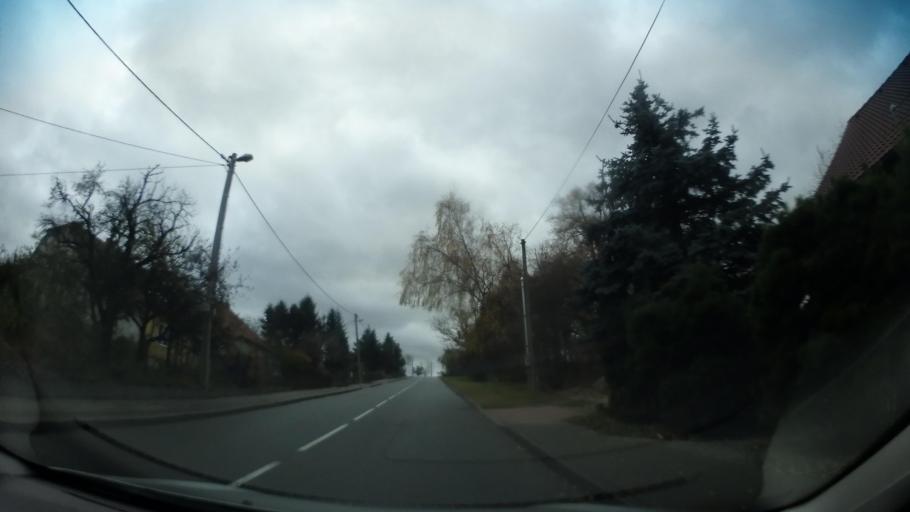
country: CZ
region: Vysocina
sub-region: Okres Zd'ar nad Sazavou
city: Velka Bites
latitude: 49.2825
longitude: 16.2266
